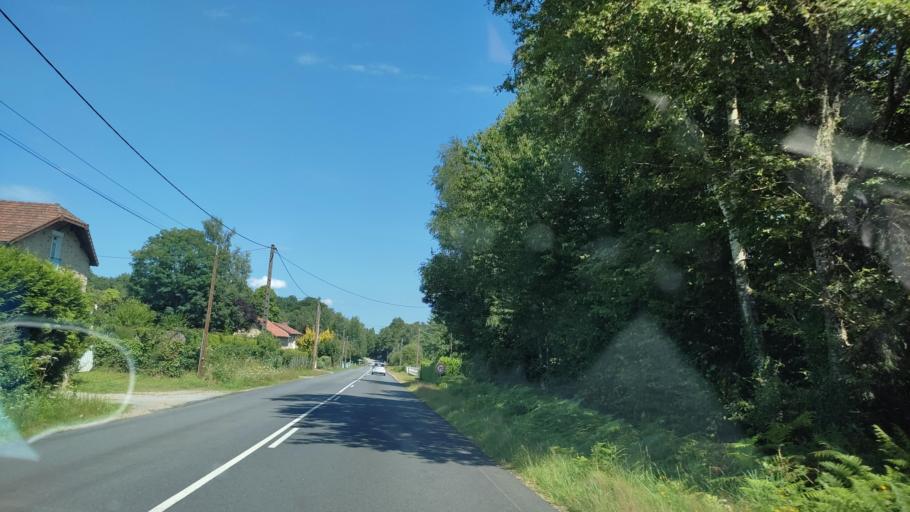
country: FR
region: Limousin
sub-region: Departement de la Haute-Vienne
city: Ambazac
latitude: 45.9401
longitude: 1.3755
